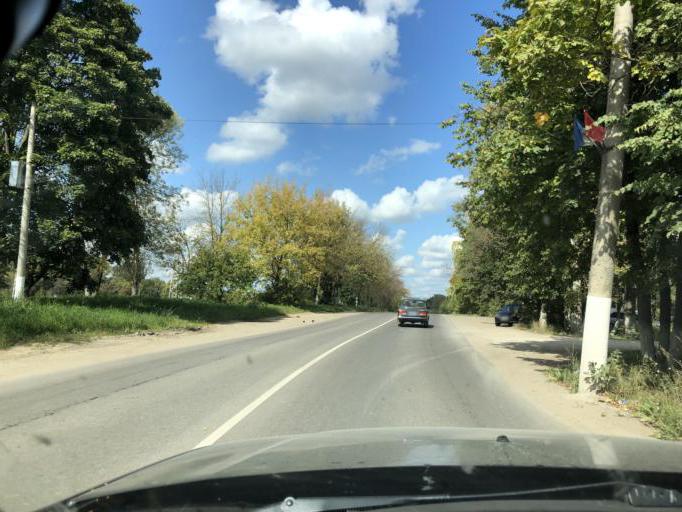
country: RU
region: Tula
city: Yasnogorsk
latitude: 54.4824
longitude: 37.6836
